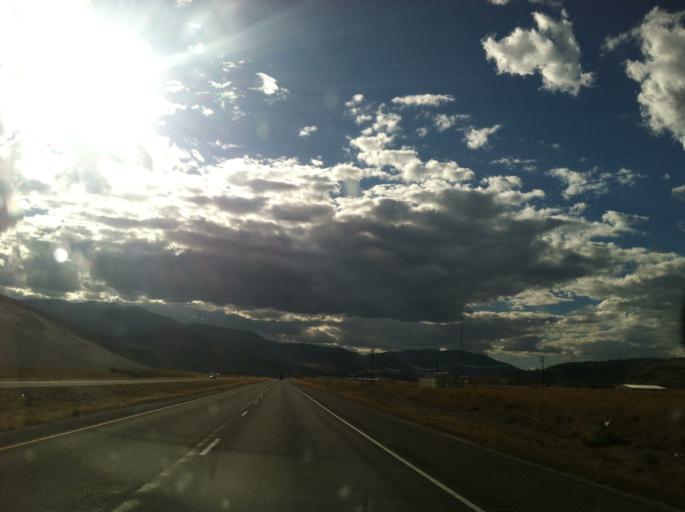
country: US
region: Montana
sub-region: Deer Lodge County
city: Anaconda
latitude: 46.1276
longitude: -112.9093
